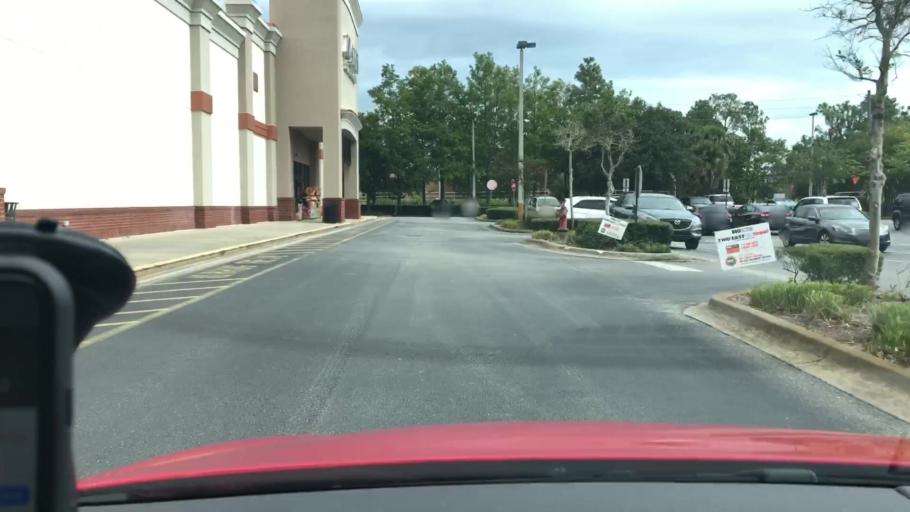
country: US
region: Florida
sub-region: Volusia County
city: Daytona Beach
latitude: 29.1819
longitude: -81.0812
